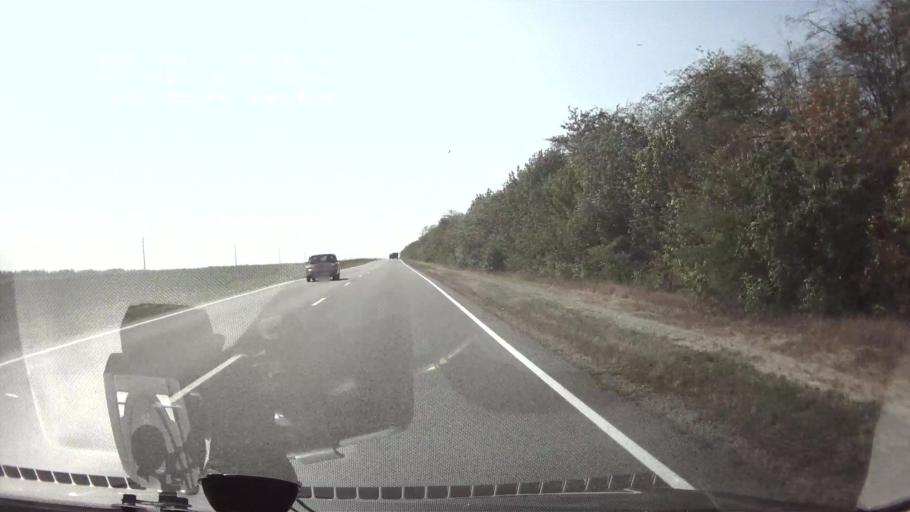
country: RU
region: Krasnodarskiy
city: Novopokrovskaya
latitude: 45.8711
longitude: 40.7205
